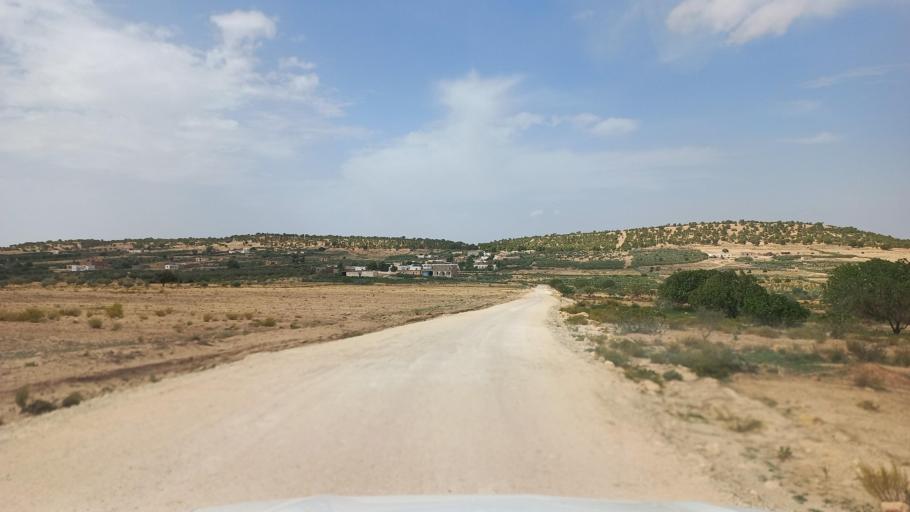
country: TN
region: Al Qasrayn
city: Kasserine
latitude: 35.3857
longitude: 8.8650
